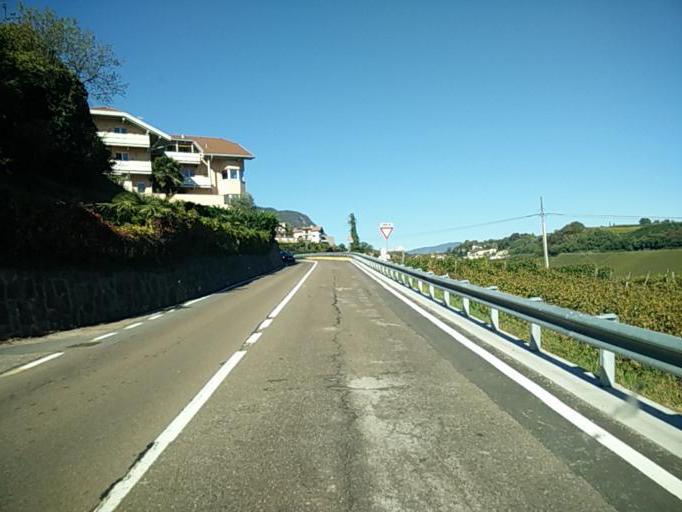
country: IT
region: Trentino-Alto Adige
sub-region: Bolzano
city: Caldaro sulla Strada del Vino
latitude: 46.4051
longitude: 11.2486
